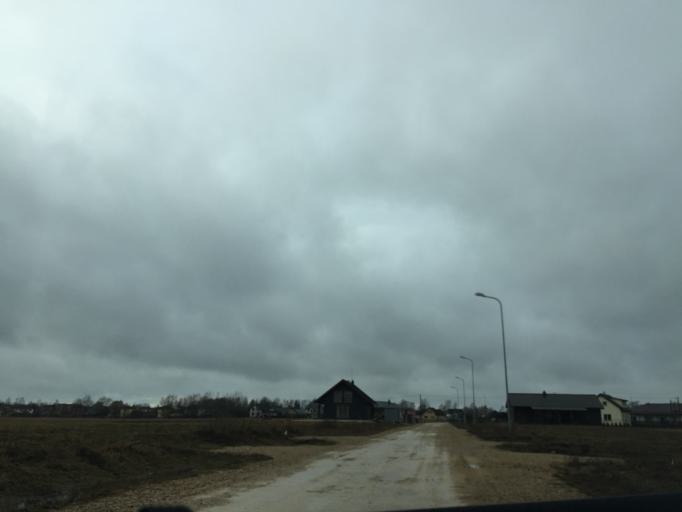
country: LV
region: Adazi
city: Adazi
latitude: 57.0672
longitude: 24.3434
